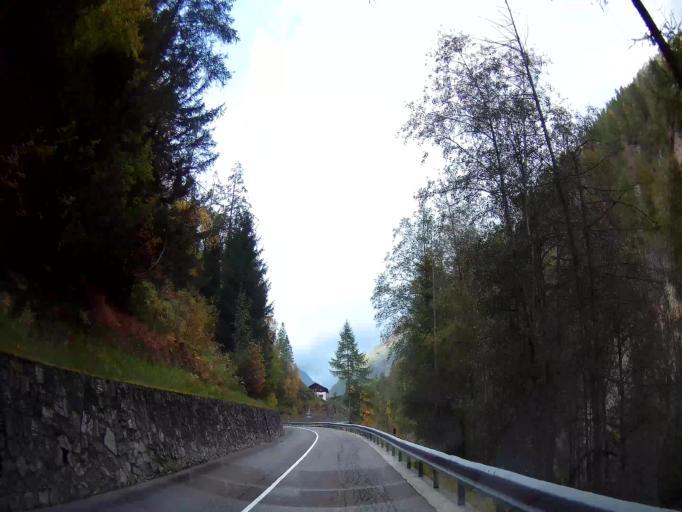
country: IT
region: Trentino-Alto Adige
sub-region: Bolzano
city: Senales
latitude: 46.7076
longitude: 10.9093
